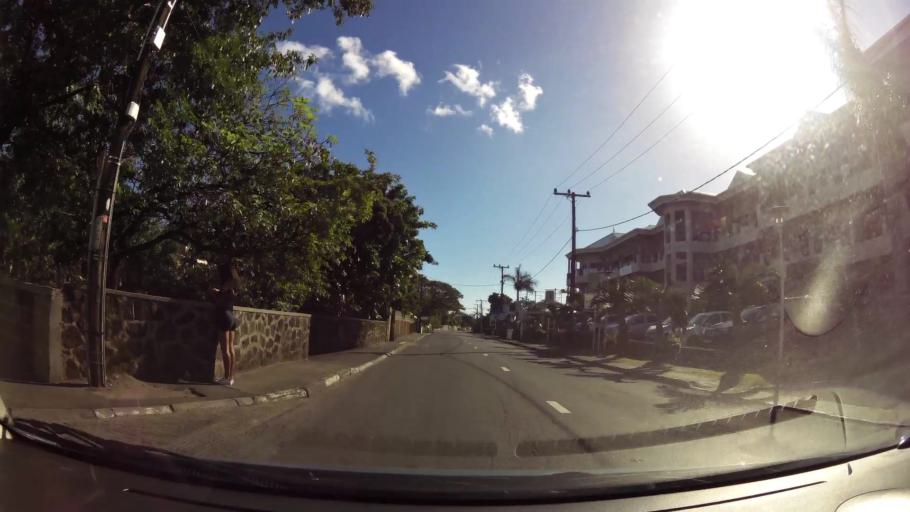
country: MU
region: Black River
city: Grande Riviere Noire
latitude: -20.3446
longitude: 57.3642
